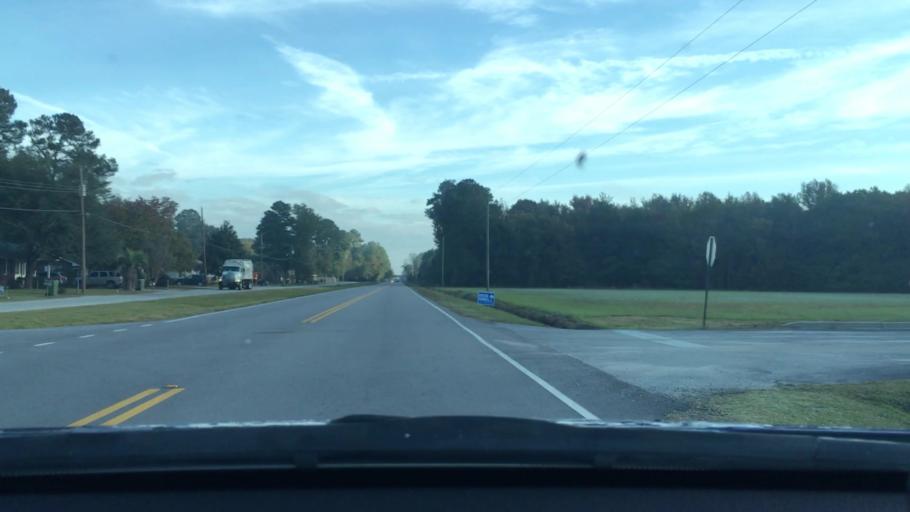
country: US
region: South Carolina
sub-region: Sumter County
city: Sumter
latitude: 33.9300
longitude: -80.3245
